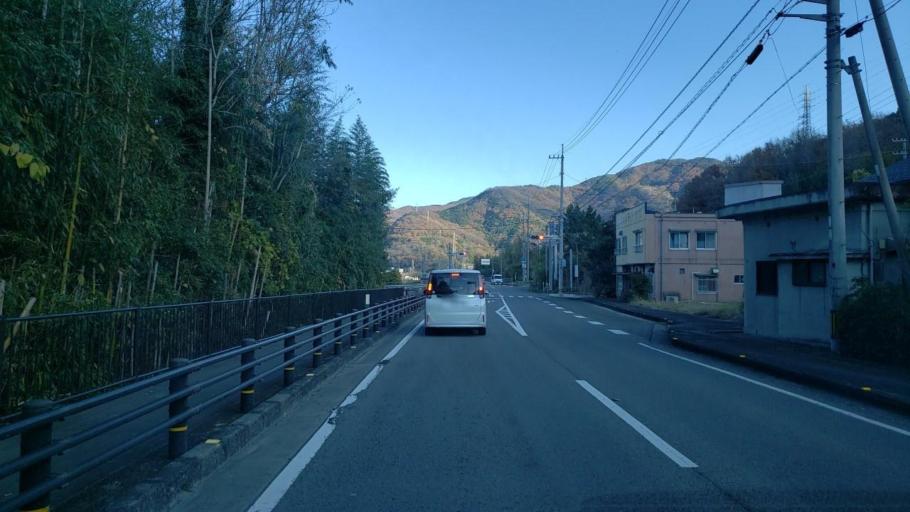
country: JP
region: Tokushima
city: Wakimachi
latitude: 34.0427
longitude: 134.0503
